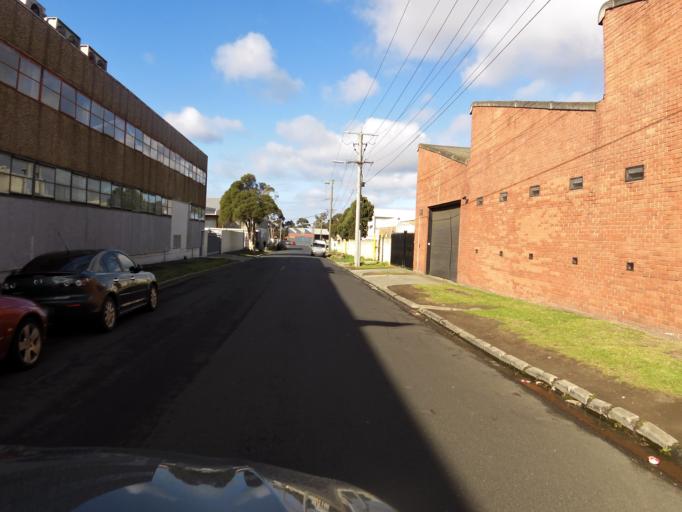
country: AU
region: Victoria
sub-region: Maribyrnong
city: Kingsville
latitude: -37.8108
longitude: 144.8615
